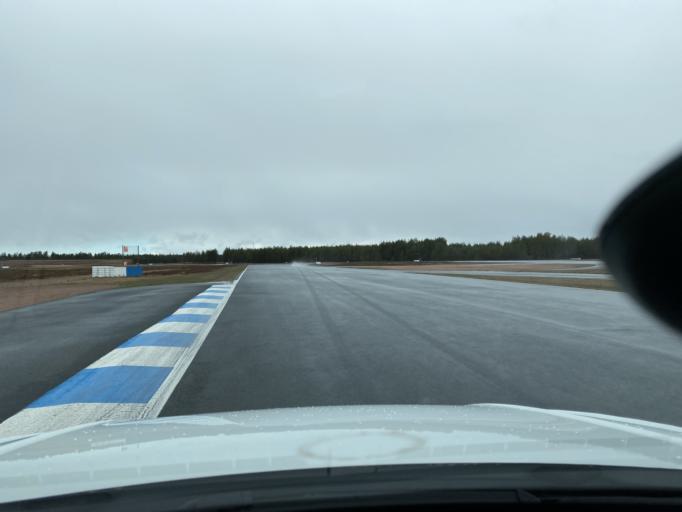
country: FI
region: Satakunta
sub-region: Pori
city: Vampula
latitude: 60.9762
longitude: 22.6697
